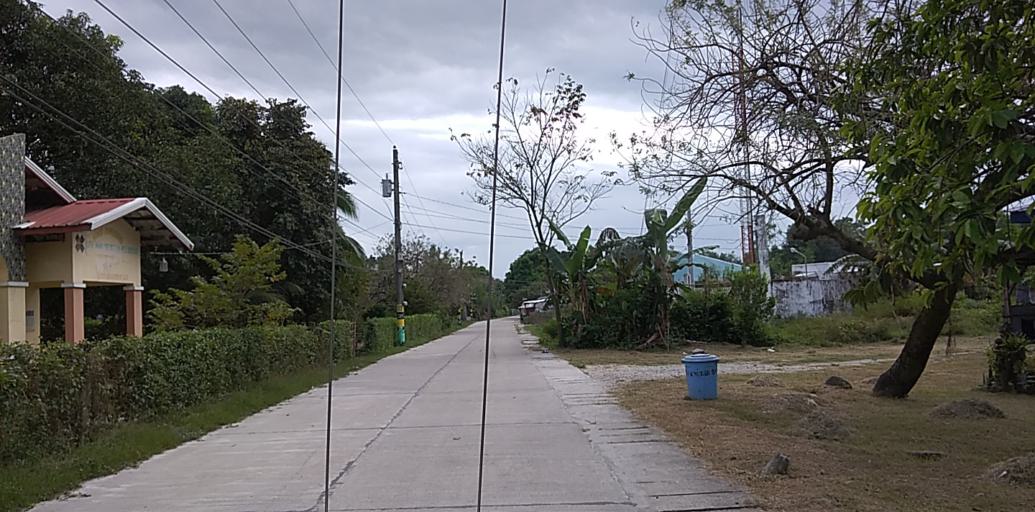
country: PH
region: Central Luzon
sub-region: Province of Pampanga
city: Pulung Santol
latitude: 15.0478
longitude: 120.5558
